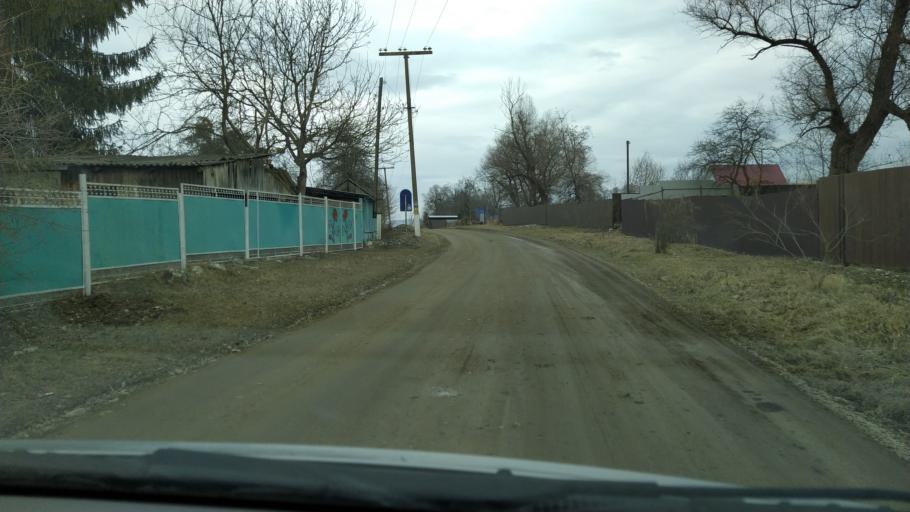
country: RU
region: Krasnodarskiy
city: Peredovaya
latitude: 44.0872
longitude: 41.3641
